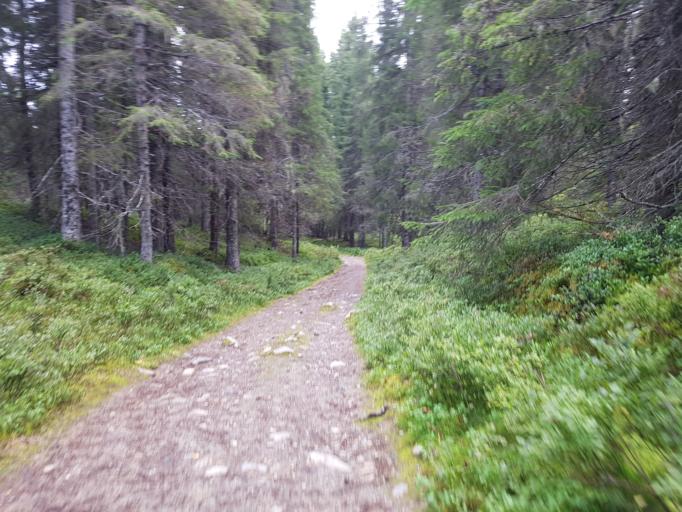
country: NO
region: Sor-Trondelag
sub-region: Trondheim
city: Trondheim
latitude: 63.4186
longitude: 10.3008
